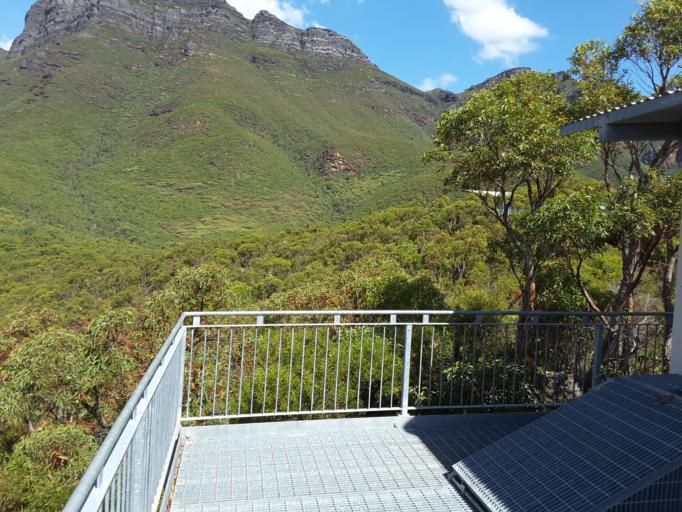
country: AU
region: Western Australia
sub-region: Plantagenet Shire
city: Kendenup
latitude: -34.3672
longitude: 118.2422
